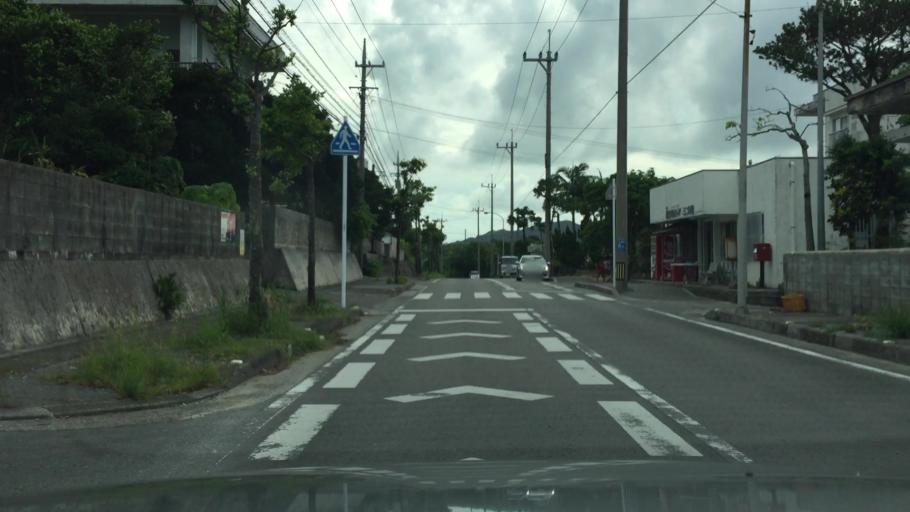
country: JP
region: Okinawa
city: Ishigaki
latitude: 24.4477
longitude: 124.1560
